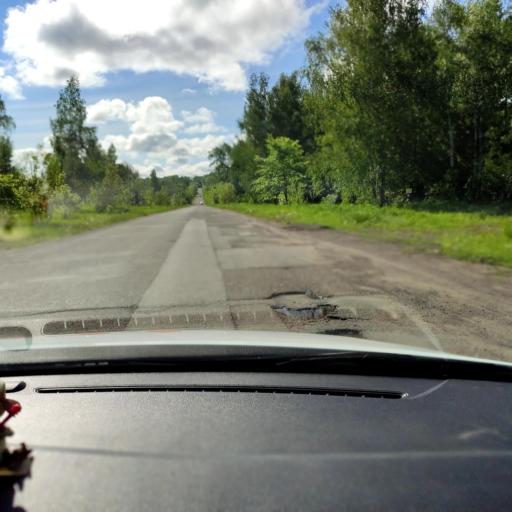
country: RU
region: Tatarstan
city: Stolbishchi
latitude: 55.7224
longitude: 49.2066
